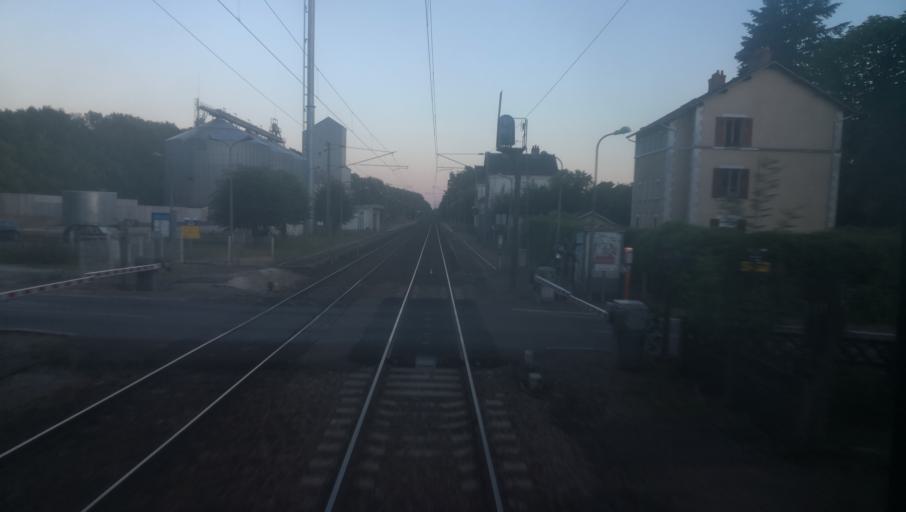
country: FR
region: Centre
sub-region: Departement du Cher
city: Saint-Satur
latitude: 47.3383
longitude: 2.8802
